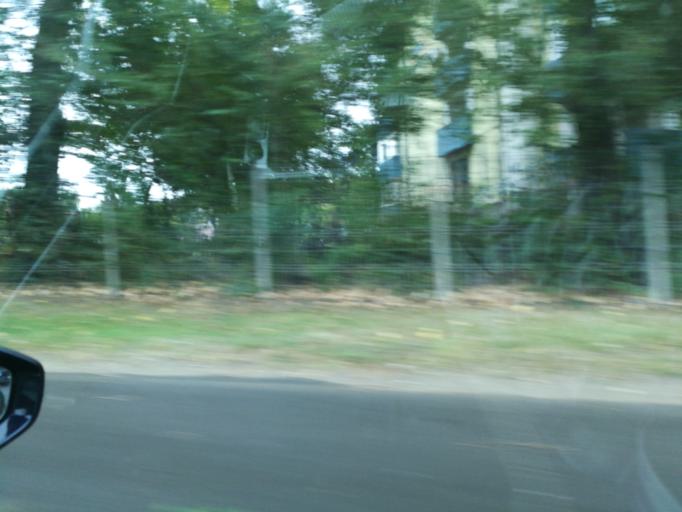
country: RO
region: Galati
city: Galati
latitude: 45.4485
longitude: 28.0138
